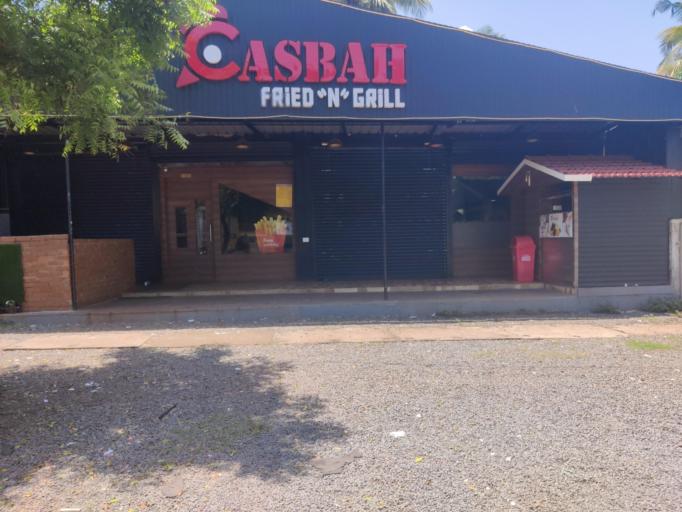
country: IN
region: Kerala
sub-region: Kasaragod District
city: Kannangad
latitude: 12.3801
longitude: 75.0509
